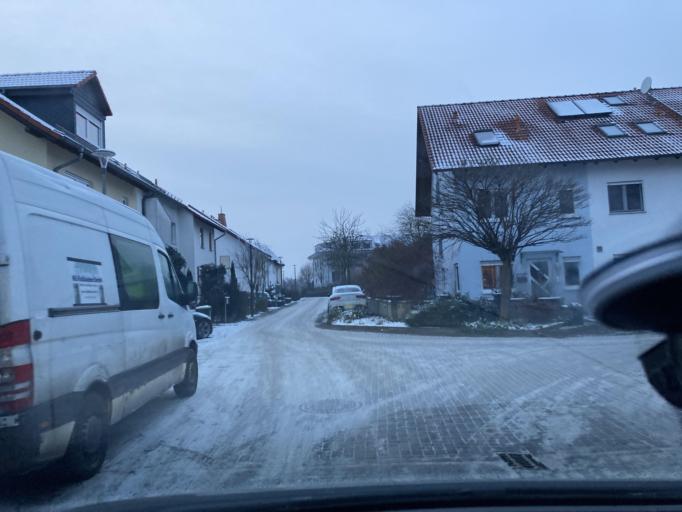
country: DE
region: Hesse
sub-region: Regierungsbezirk Darmstadt
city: Offenbach
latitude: 50.1307
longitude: 8.7942
